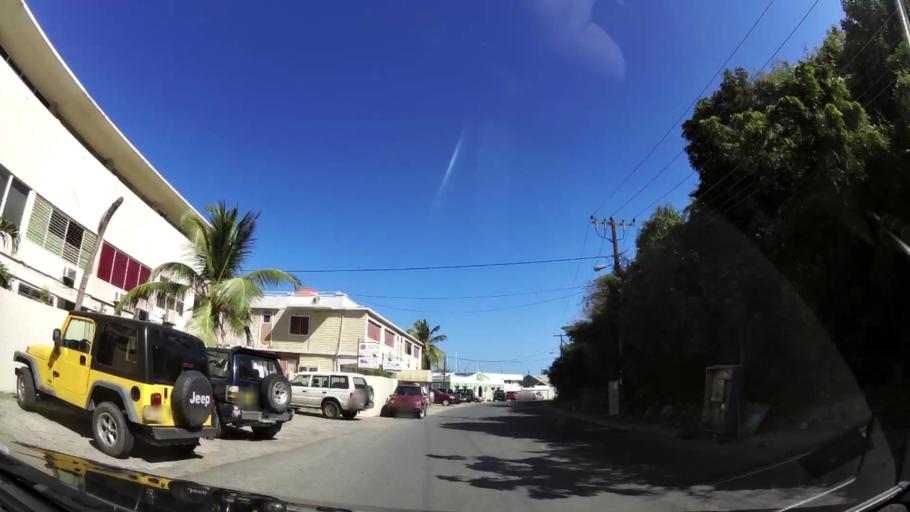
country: VG
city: Road Town
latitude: 18.4139
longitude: -64.6156
